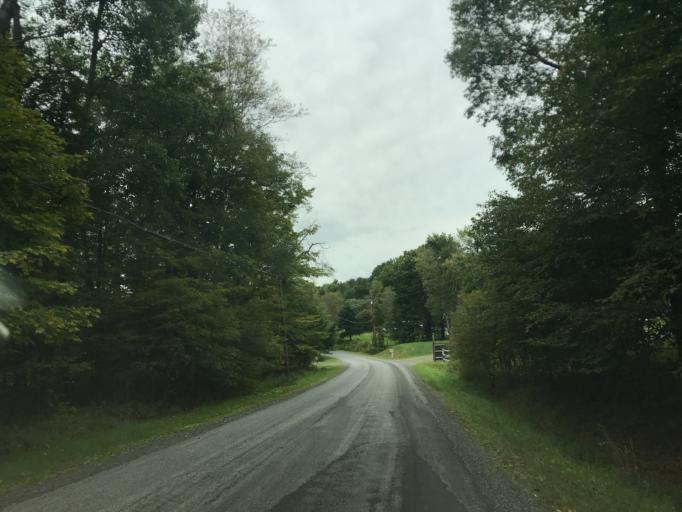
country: US
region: New York
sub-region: Otsego County
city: Worcester
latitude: 42.5172
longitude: -74.6652
